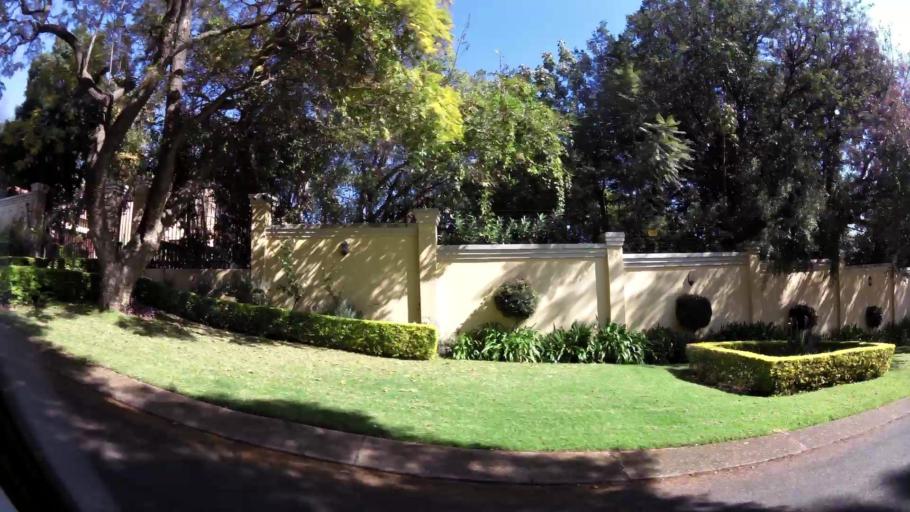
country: ZA
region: Gauteng
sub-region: City of Tshwane Metropolitan Municipality
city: Pretoria
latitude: -25.7807
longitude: 28.2350
